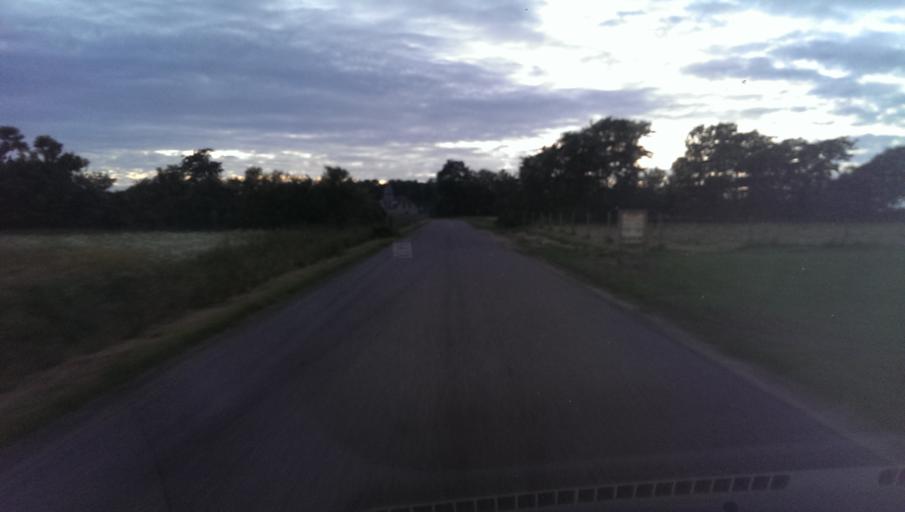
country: DK
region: South Denmark
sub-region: Esbjerg Kommune
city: Esbjerg
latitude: 55.5318
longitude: 8.4850
